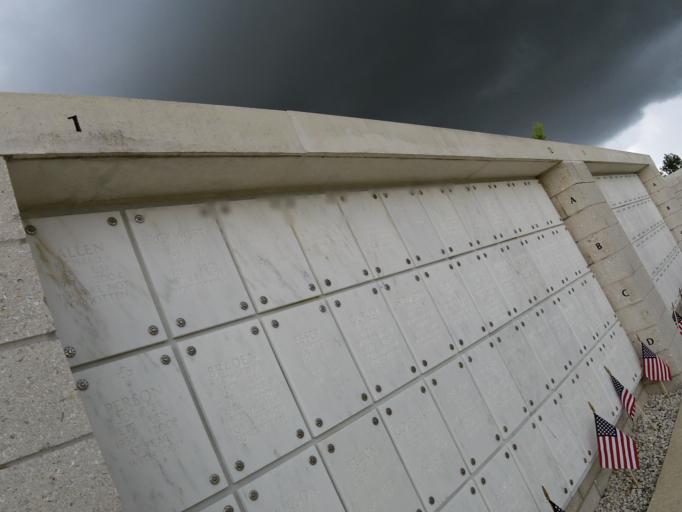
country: US
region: Florida
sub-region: Nassau County
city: Nassau Village-Ratliff
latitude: 30.5474
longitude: -81.7200
